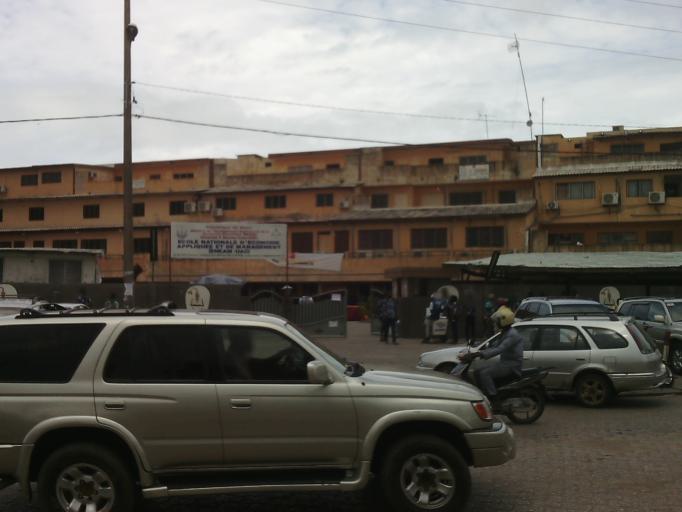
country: BJ
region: Littoral
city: Cotonou
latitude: 6.3648
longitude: 2.4085
